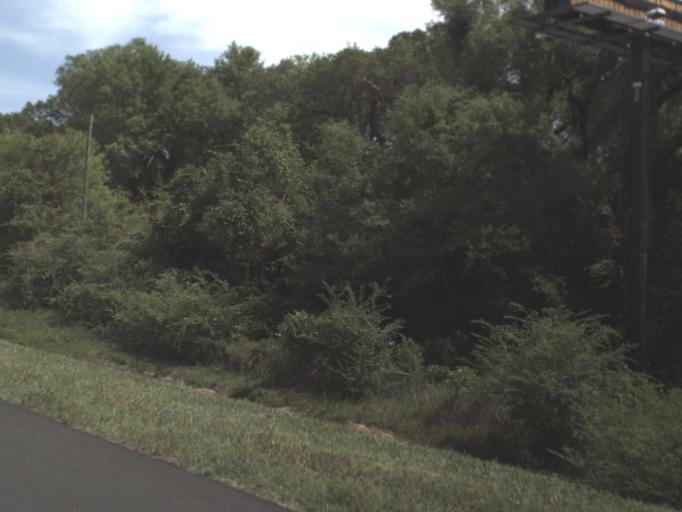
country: US
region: Florida
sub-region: Escambia County
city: Ferry Pass
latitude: 30.5318
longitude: -87.2127
